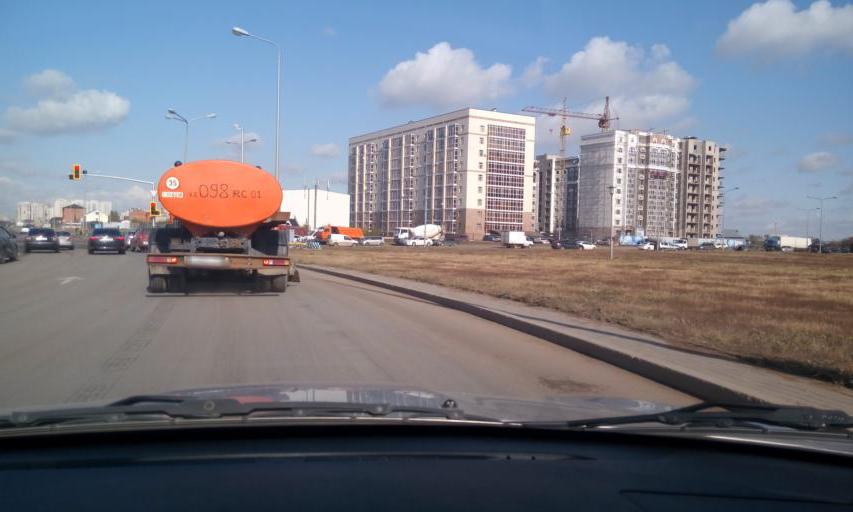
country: KZ
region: Astana Qalasy
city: Astana
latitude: 51.1254
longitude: 71.4872
